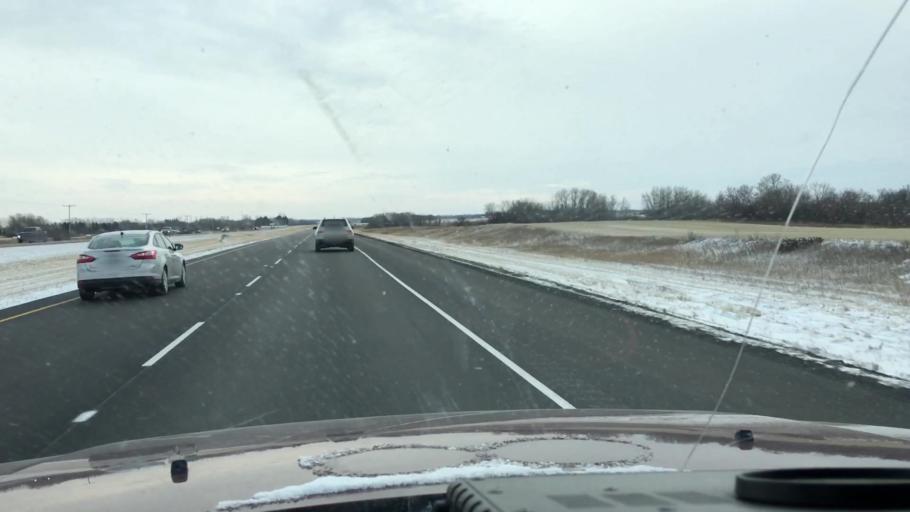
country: CA
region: Saskatchewan
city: Saskatoon
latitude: 52.0248
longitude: -106.5805
